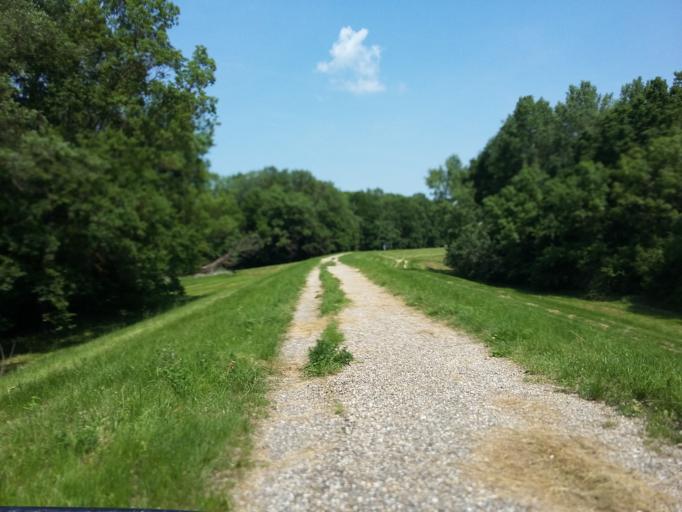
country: AT
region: Lower Austria
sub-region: Politischer Bezirk Ganserndorf
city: Angern an der March
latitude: 48.4093
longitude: 16.8557
